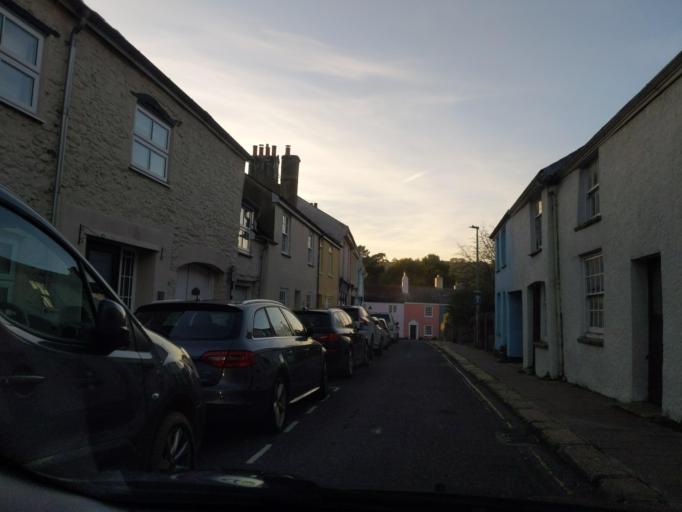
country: GB
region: England
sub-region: Devon
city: South Brent
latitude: 50.4267
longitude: -3.8352
